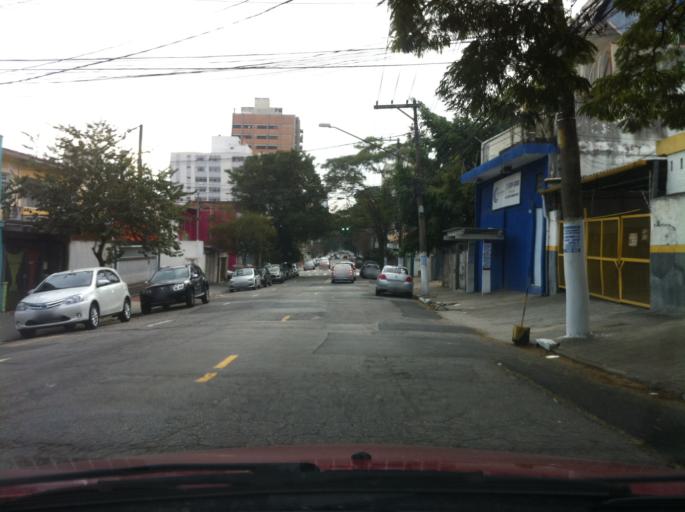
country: BR
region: Sao Paulo
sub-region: Diadema
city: Diadema
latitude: -23.6333
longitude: -46.6937
